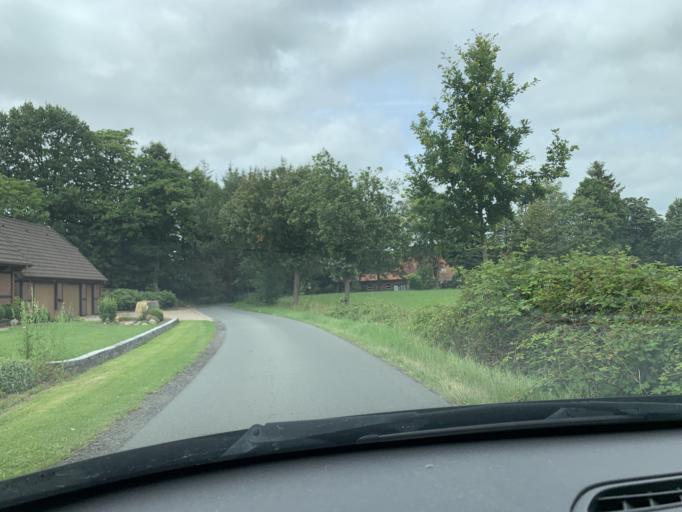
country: DE
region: Lower Saxony
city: Westerstede
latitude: 53.2696
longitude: 7.9474
